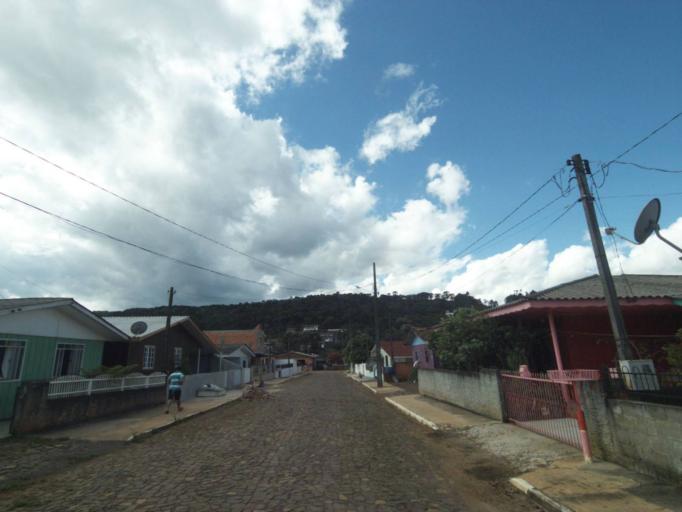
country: BR
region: Parana
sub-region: Uniao Da Vitoria
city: Uniao da Vitoria
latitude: -26.1512
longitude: -51.5426
